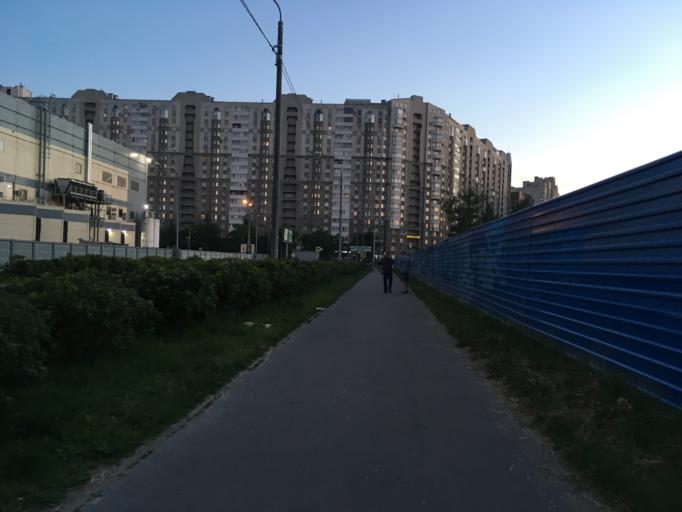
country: RU
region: Leningrad
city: Chernaya Rechka
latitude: 60.0061
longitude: 30.2992
